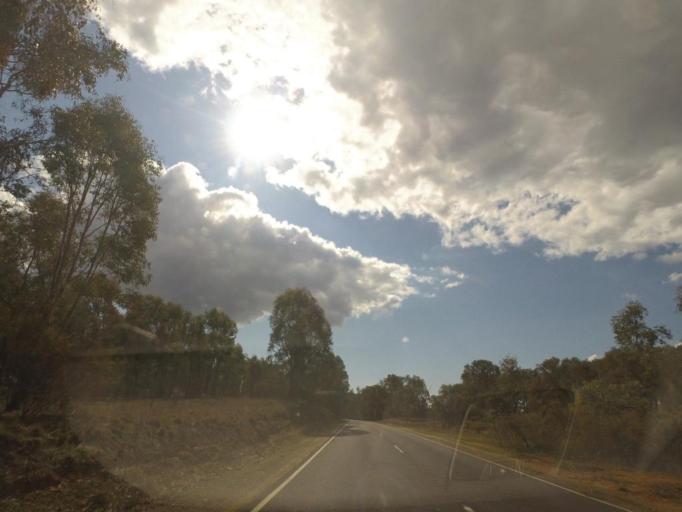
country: AU
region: New South Wales
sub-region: Corowa Shire
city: Howlong
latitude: -36.1742
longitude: 146.6078
